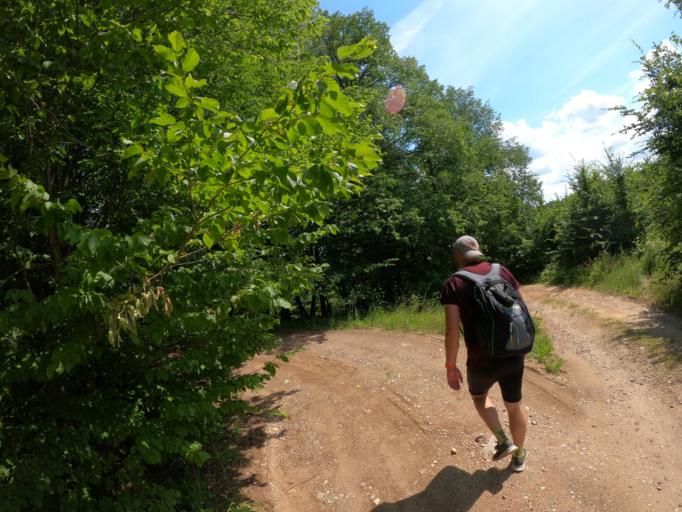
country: LT
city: Veisiejai
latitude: 54.0854
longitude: 23.5851
